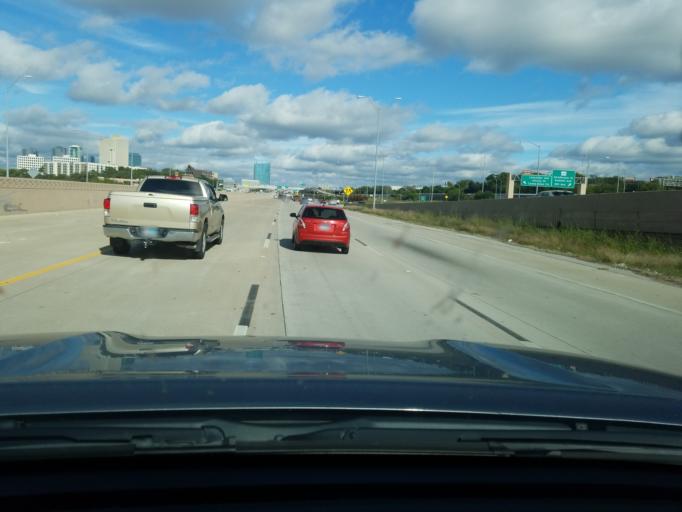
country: US
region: Texas
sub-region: Tarrant County
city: Fort Worth
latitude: 32.7389
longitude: -97.3499
